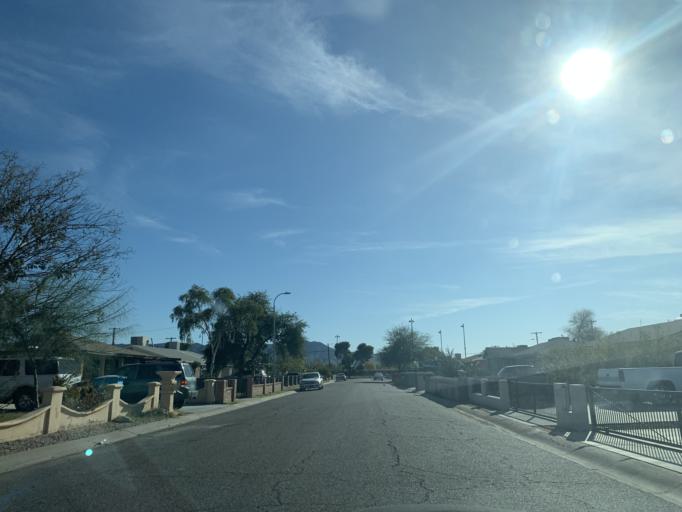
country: US
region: Arizona
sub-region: Maricopa County
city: Laveen
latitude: 33.4008
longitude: -112.1375
